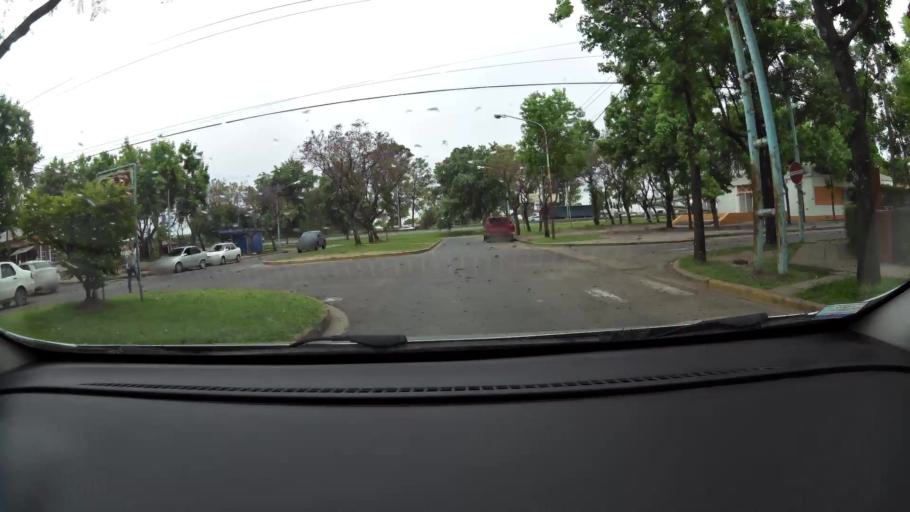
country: AR
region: Buenos Aires
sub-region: Partido de Campana
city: Campana
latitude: -34.1948
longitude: -58.9425
